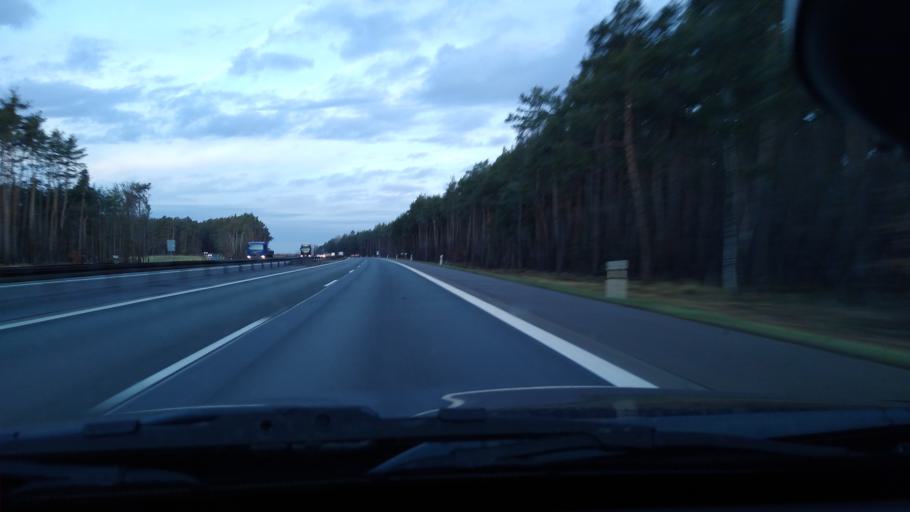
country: DE
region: Bavaria
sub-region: Regierungsbezirk Mittelfranken
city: Grossenseebach
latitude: 49.6603
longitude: 10.8925
